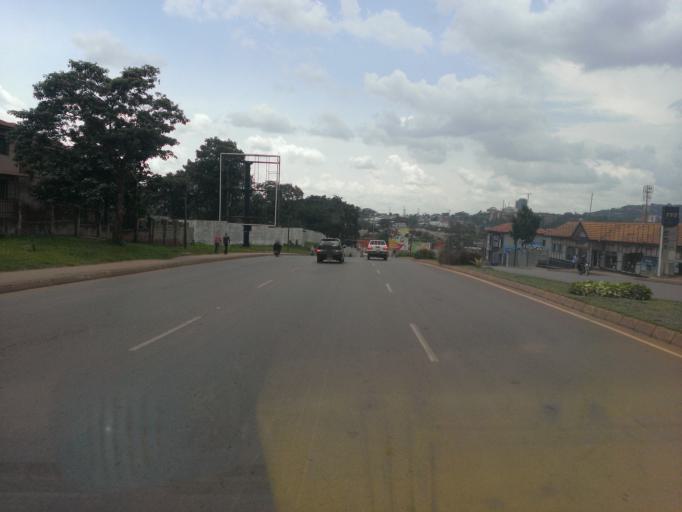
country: UG
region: Central Region
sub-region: Kampala District
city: Kampala
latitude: 0.3243
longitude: 32.6030
